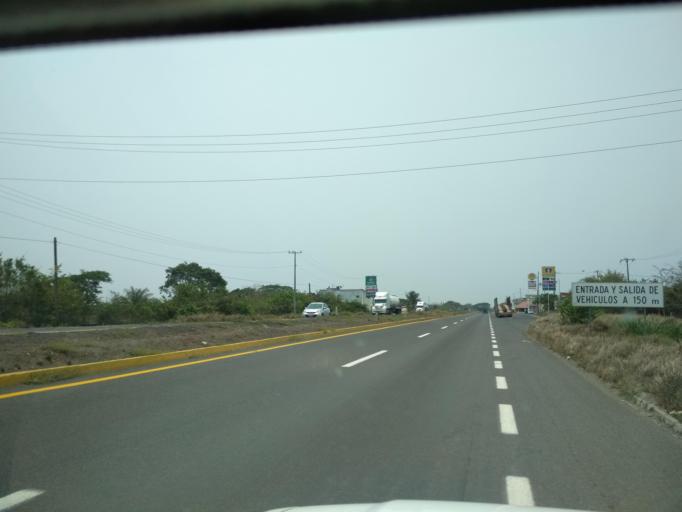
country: MX
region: Veracruz
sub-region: Veracruz
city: Delfino Victoria (Santa Fe)
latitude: 19.2206
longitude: -96.2581
